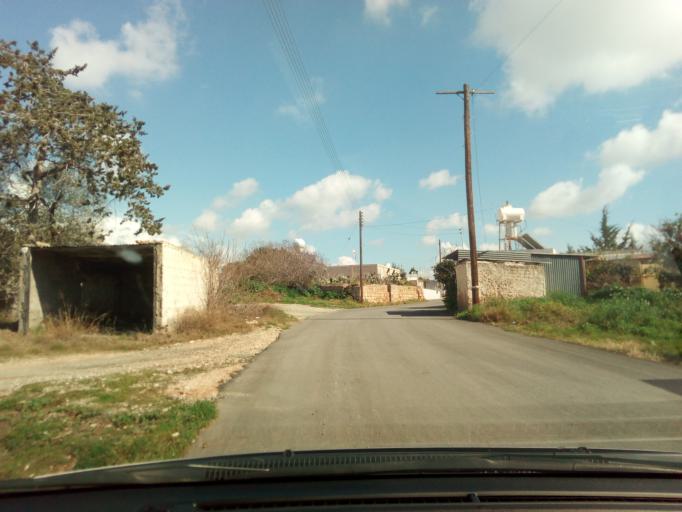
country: CY
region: Pafos
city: Empa
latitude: 34.8071
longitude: 32.4270
